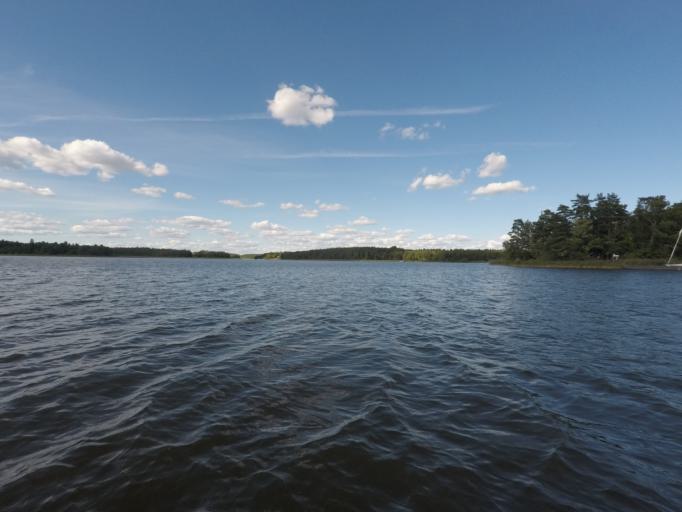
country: SE
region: Soedermanland
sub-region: Eskilstuna Kommun
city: Torshalla
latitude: 59.4753
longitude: 16.4481
